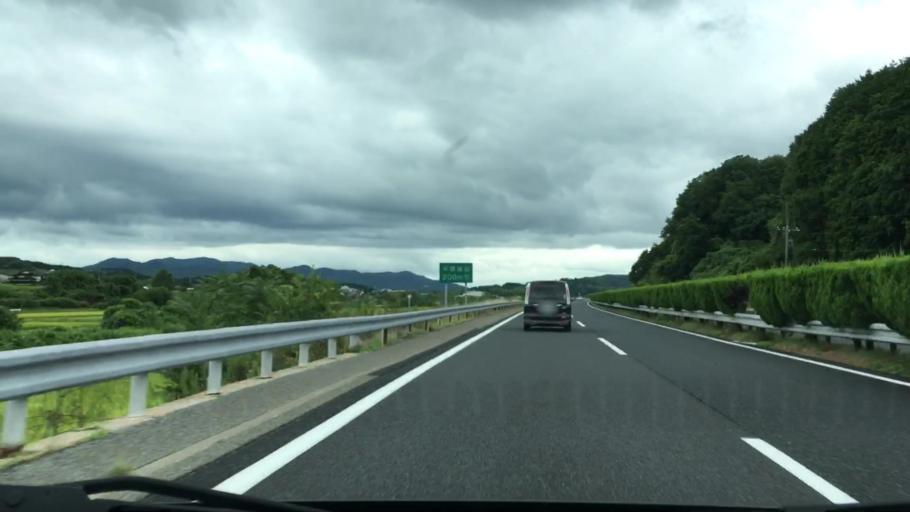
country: JP
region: Okayama
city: Tsuyama
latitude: 35.0449
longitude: 134.0824
